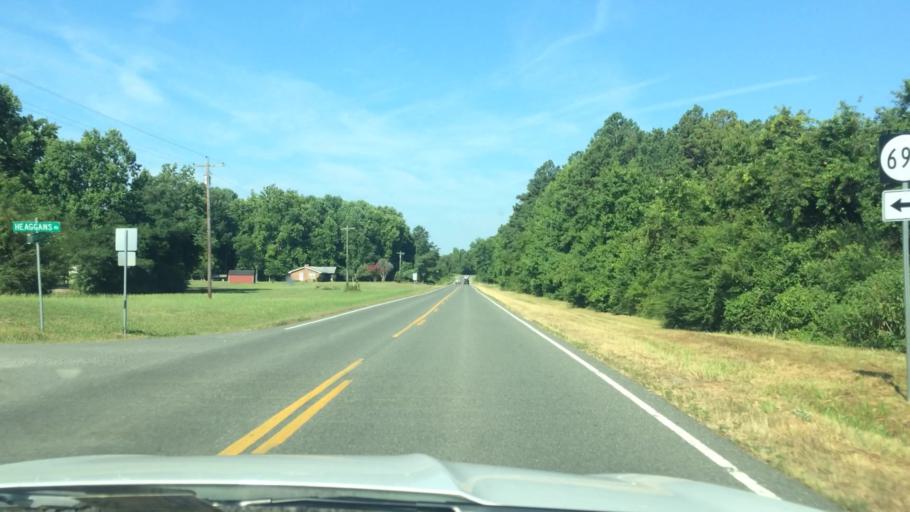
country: US
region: Virginia
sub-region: Northumberland County
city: Heathsville
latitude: 37.8511
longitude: -76.5910
